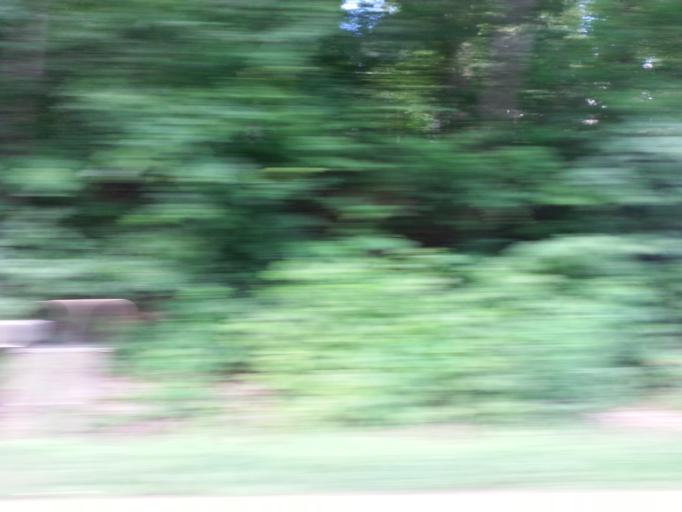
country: US
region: Tennessee
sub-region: Loudon County
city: Greenback
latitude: 35.6065
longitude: -84.0867
